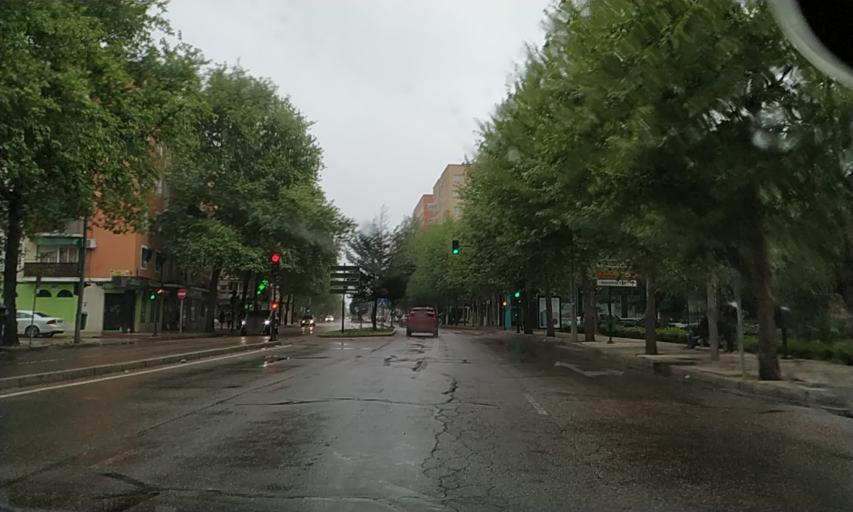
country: ES
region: Extremadura
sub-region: Provincia de Badajoz
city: Badajoz
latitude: 38.8681
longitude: -6.9732
